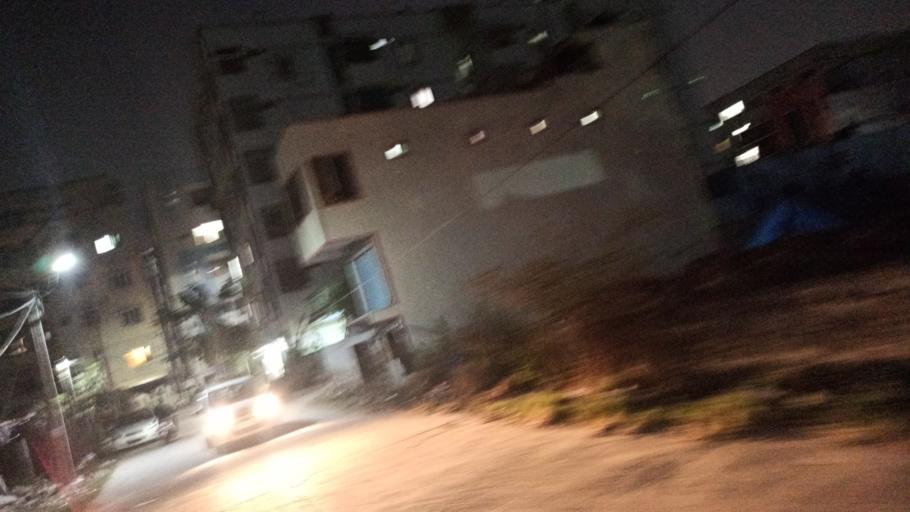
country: IN
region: Telangana
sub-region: Rangareddi
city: Kukatpalli
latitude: 17.5222
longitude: 78.3906
